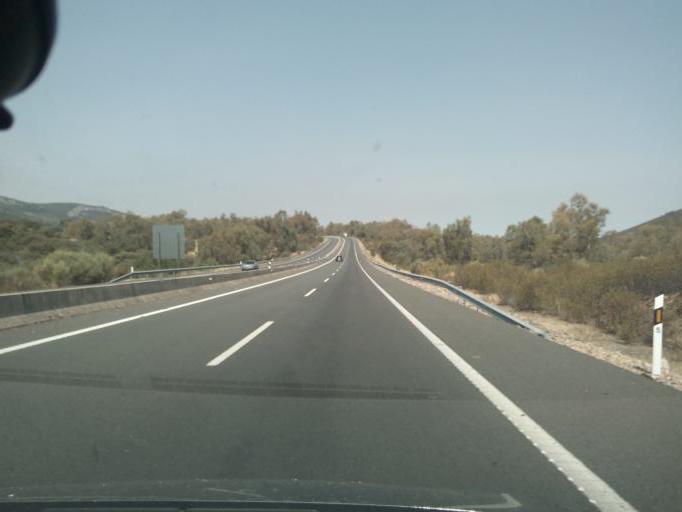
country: ES
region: Extremadura
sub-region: Provincia de Caceres
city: Higuera
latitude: 39.7105
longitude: -5.6935
